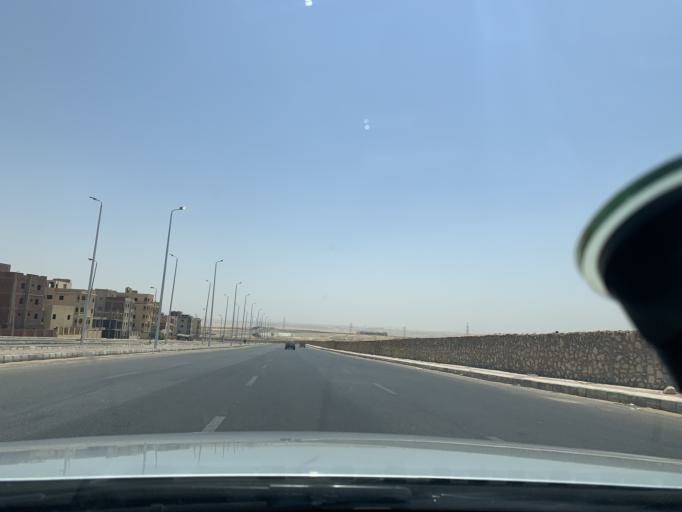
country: EG
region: Muhafazat al Qahirah
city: Halwan
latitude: 29.9824
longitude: 31.4686
